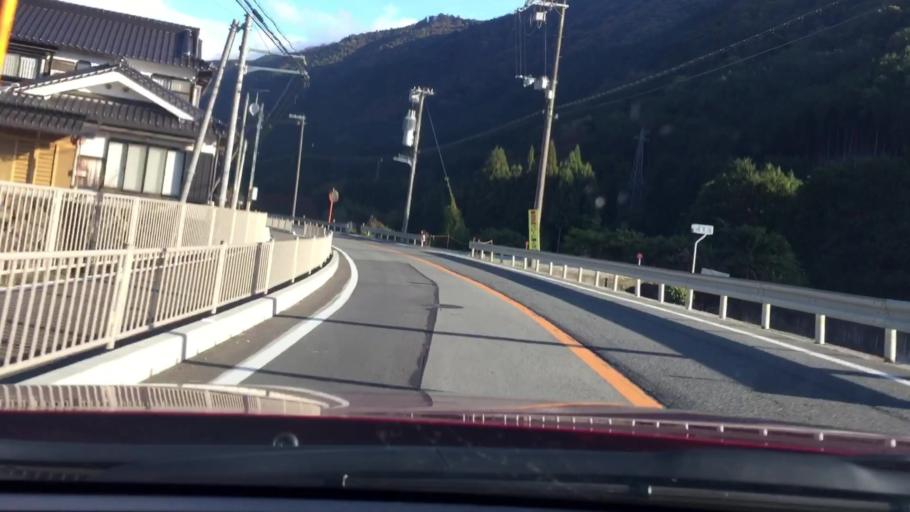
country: JP
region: Hyogo
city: Yamazakicho-nakabirose
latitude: 35.1203
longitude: 134.5690
